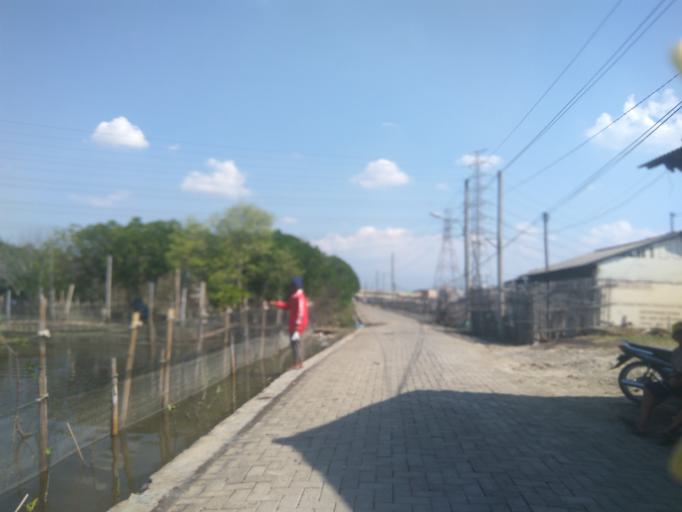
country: ID
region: Central Java
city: Semarang
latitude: -6.9480
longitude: 110.4408
